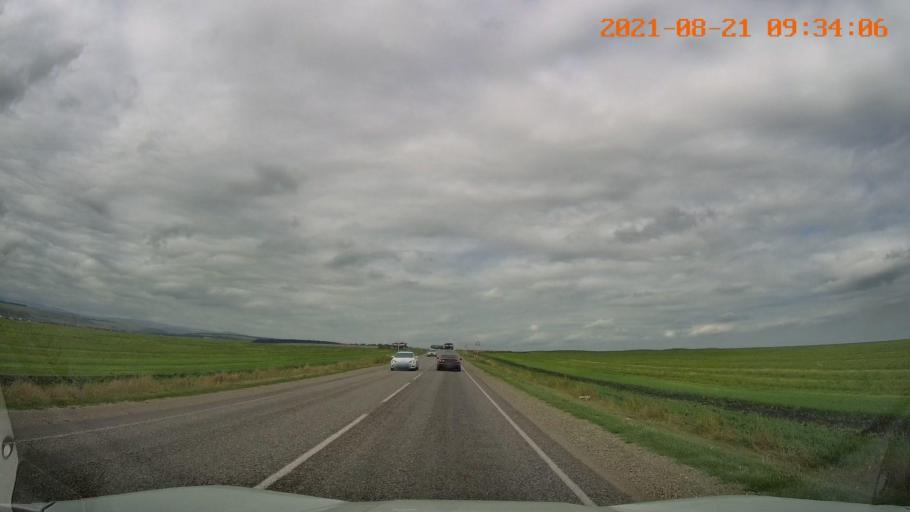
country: RU
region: Stavropol'skiy
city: Yutsa
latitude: 43.9925
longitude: 42.9776
